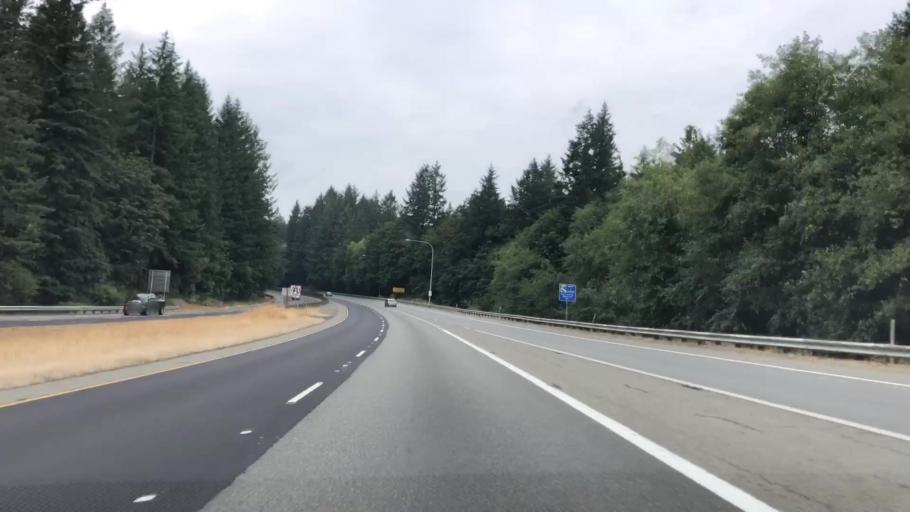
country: US
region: Washington
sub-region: Kitsap County
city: Navy Yard City
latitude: 47.5244
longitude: -122.6609
